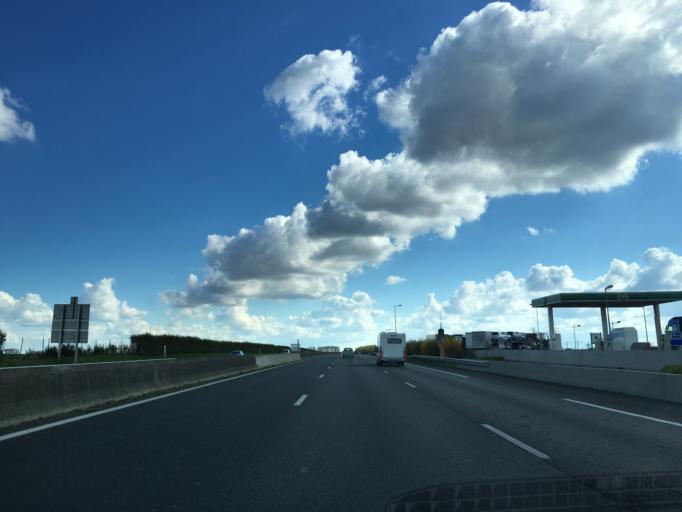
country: FR
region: Nord-Pas-de-Calais
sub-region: Departement du Pas-de-Calais
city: Croisilles
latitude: 50.1744
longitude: 2.8744
